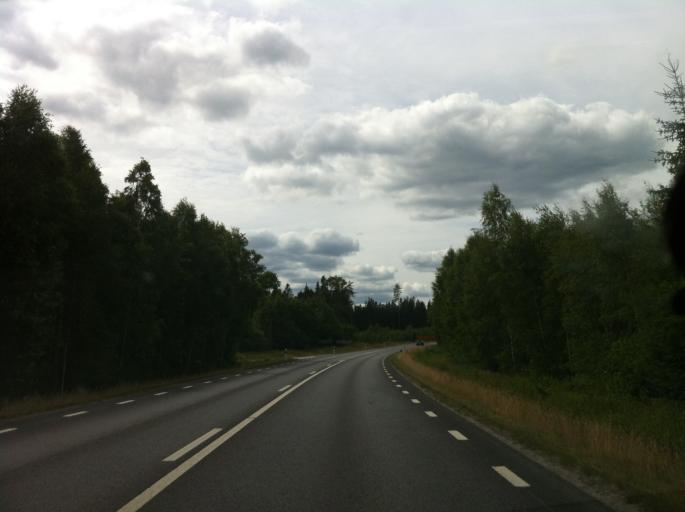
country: SE
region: Kronoberg
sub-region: Tingsryds Kommun
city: Tingsryd
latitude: 56.5266
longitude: 14.9243
